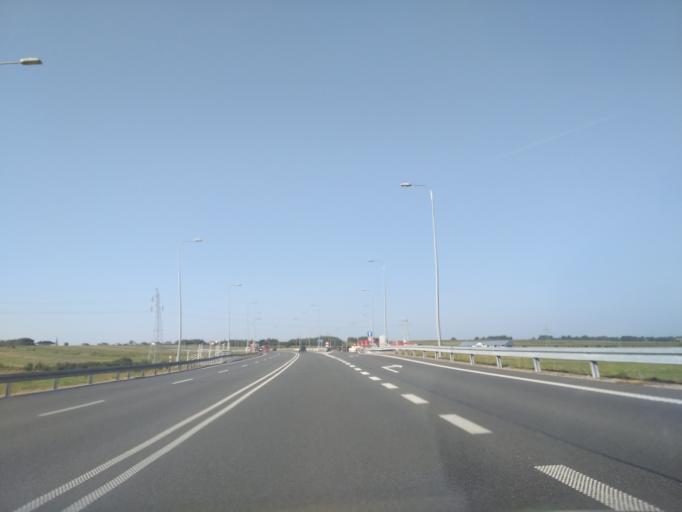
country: PL
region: Subcarpathian Voivodeship
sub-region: Powiat rzeszowski
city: Sokolow Malopolski
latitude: 50.2066
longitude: 22.1111
